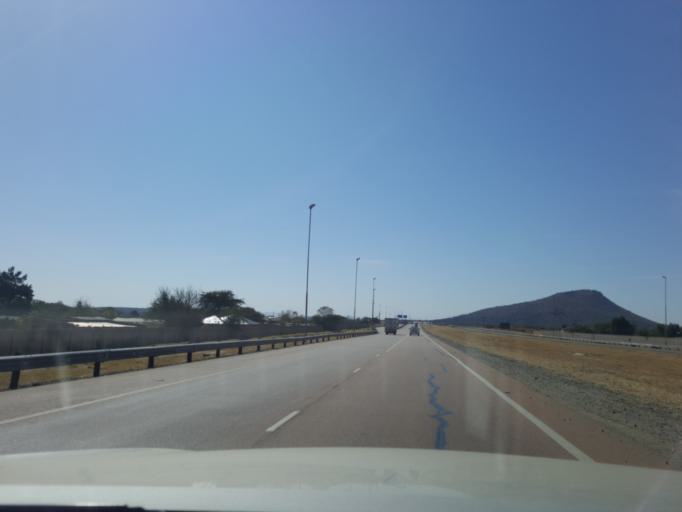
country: ZA
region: North-West
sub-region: Bojanala Platinum District Municipality
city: Brits
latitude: -25.7243
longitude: 27.6754
